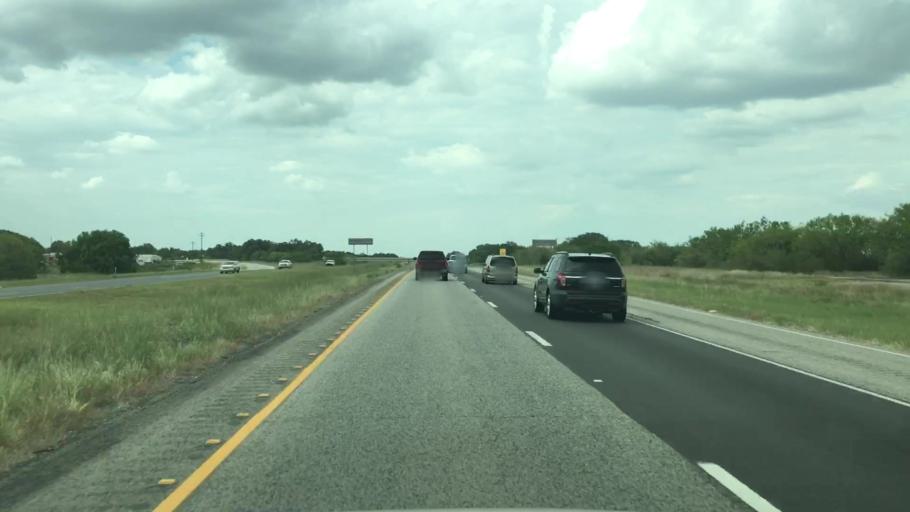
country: US
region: Texas
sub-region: Atascosa County
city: Pleasanton
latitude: 29.0462
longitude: -98.4316
